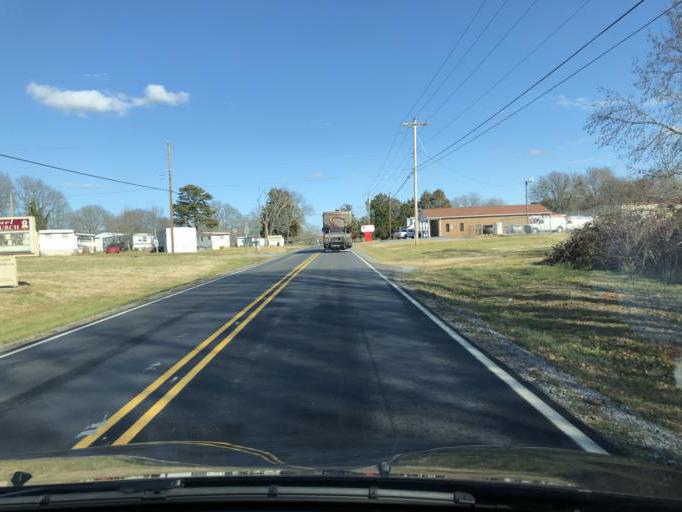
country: US
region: North Carolina
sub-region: Cleveland County
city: Shelby
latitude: 35.2259
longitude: -81.5266
